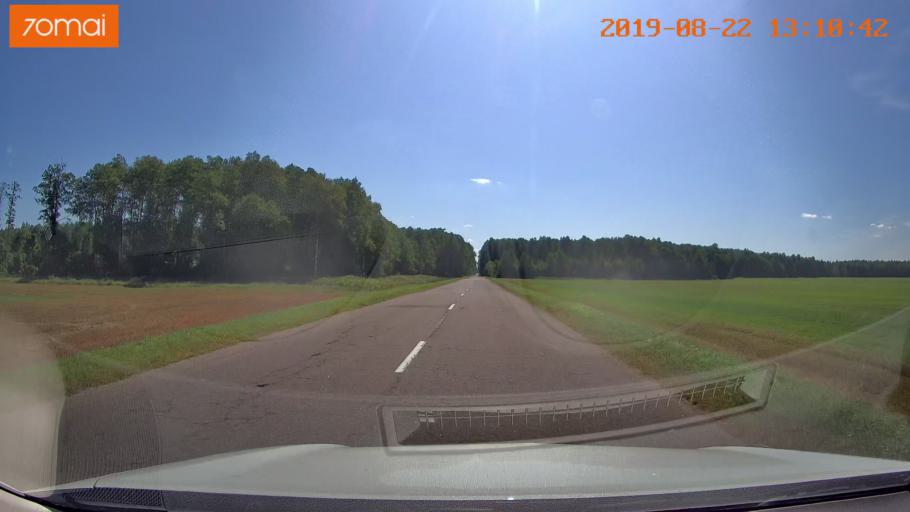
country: BY
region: Minsk
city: Prawdzinski
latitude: 53.2913
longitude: 27.8500
